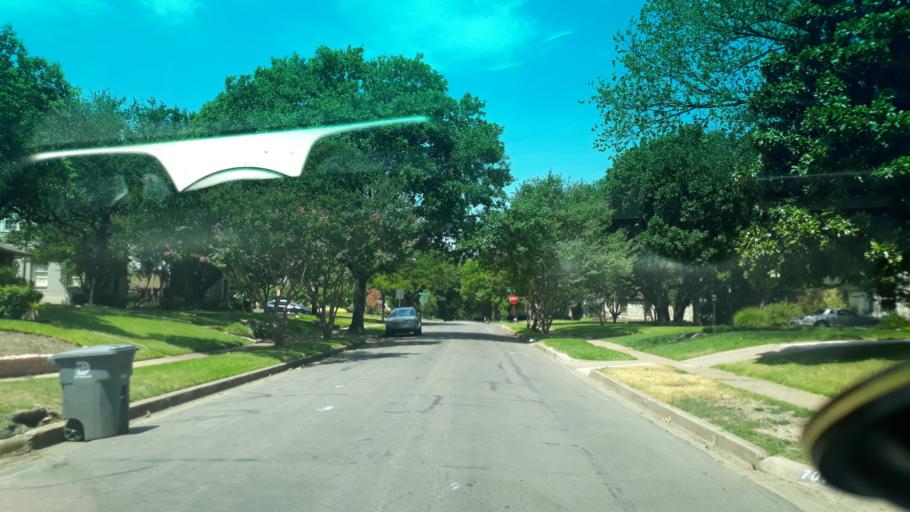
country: US
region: Texas
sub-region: Dallas County
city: Highland Park
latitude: 32.8127
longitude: -96.7373
